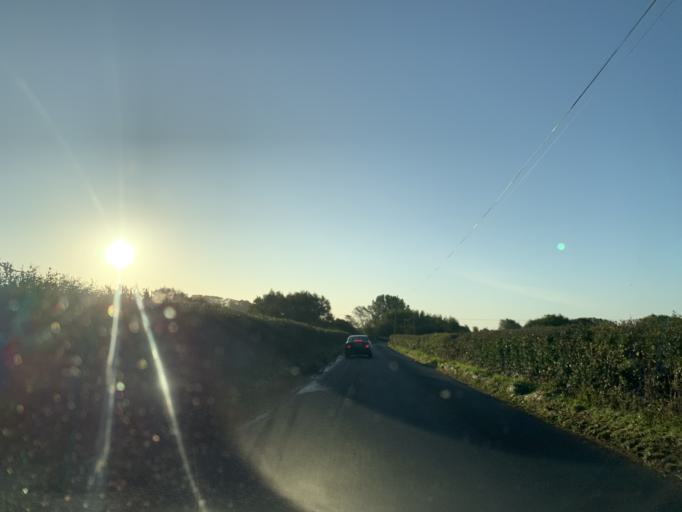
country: GB
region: England
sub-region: Wiltshire
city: Woodford
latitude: 51.0972
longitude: -1.8206
